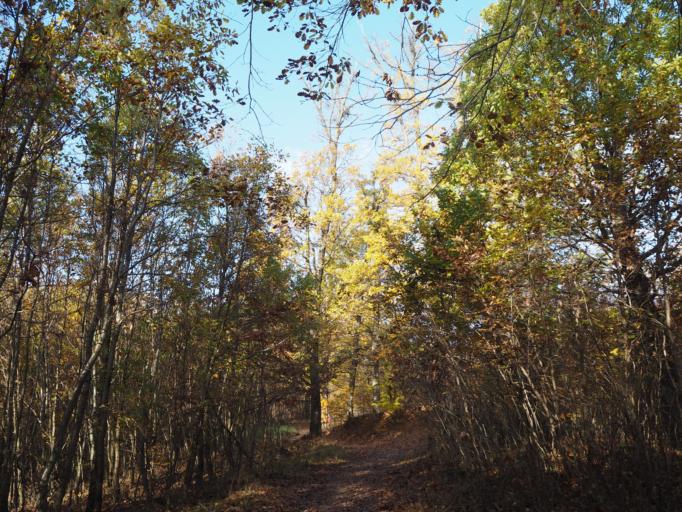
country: HU
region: Baranya
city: Hosszuheteny
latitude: 46.1887
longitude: 18.3749
